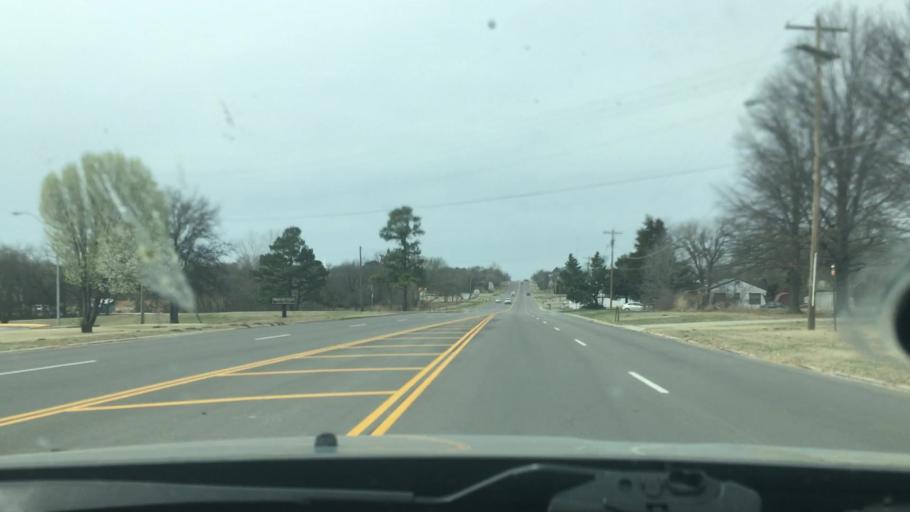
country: US
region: Oklahoma
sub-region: Seminole County
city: Seminole
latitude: 35.2496
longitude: -96.7033
